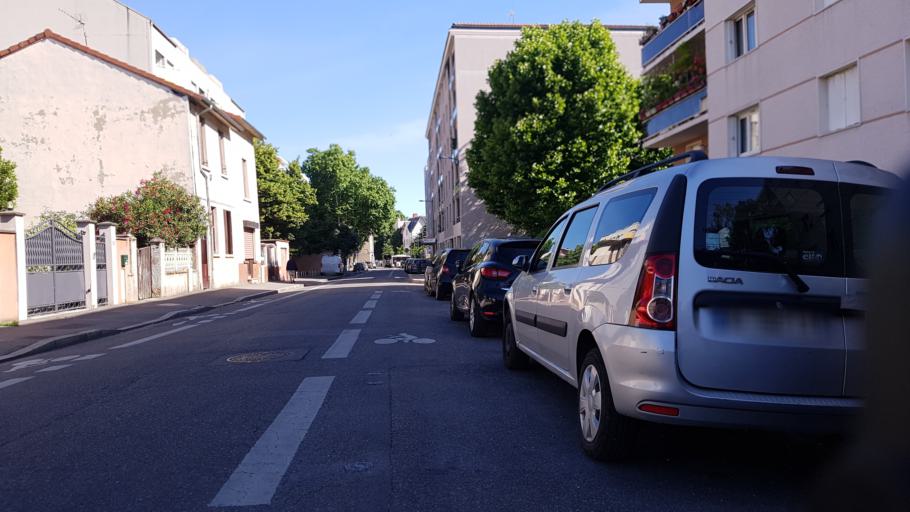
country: FR
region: Rhone-Alpes
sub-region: Departement du Rhone
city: Villeurbanne
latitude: 45.7764
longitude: 4.8842
